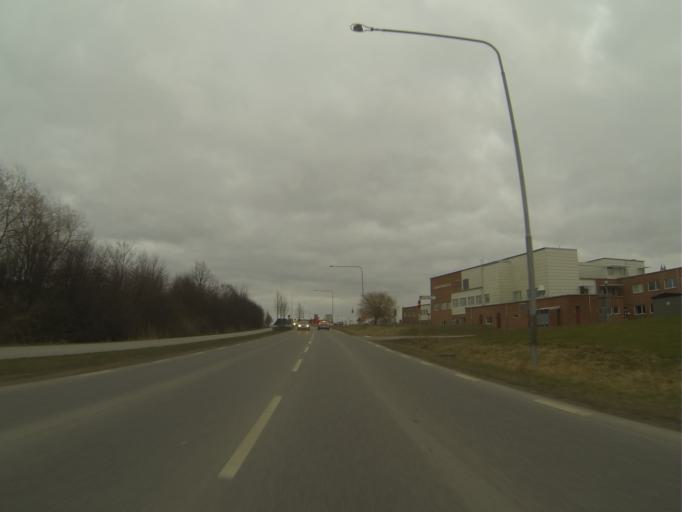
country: SE
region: Skane
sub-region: Svedala Kommun
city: Svedala
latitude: 55.5162
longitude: 13.2311
